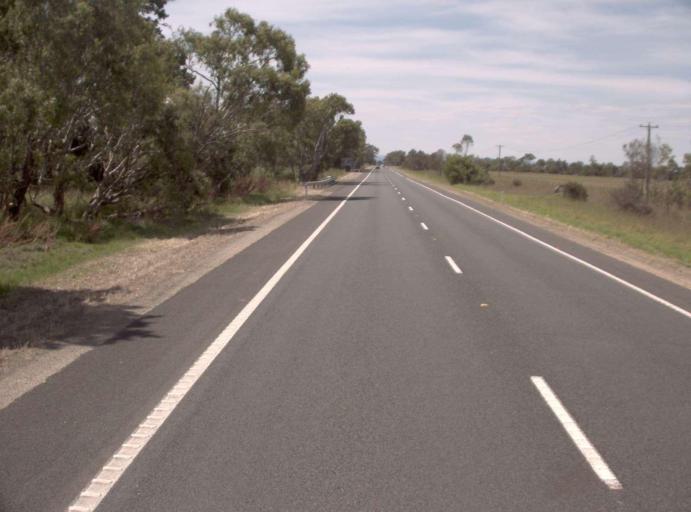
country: AU
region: Victoria
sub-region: Wellington
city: Sale
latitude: -38.0087
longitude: 147.0624
